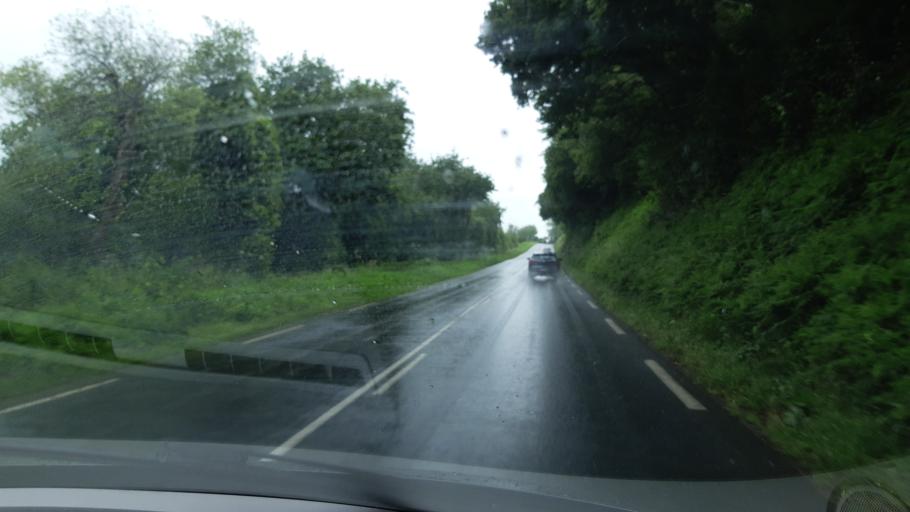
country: FR
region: Brittany
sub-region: Departement du Finistere
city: Plougoulm
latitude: 48.6545
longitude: -4.0352
